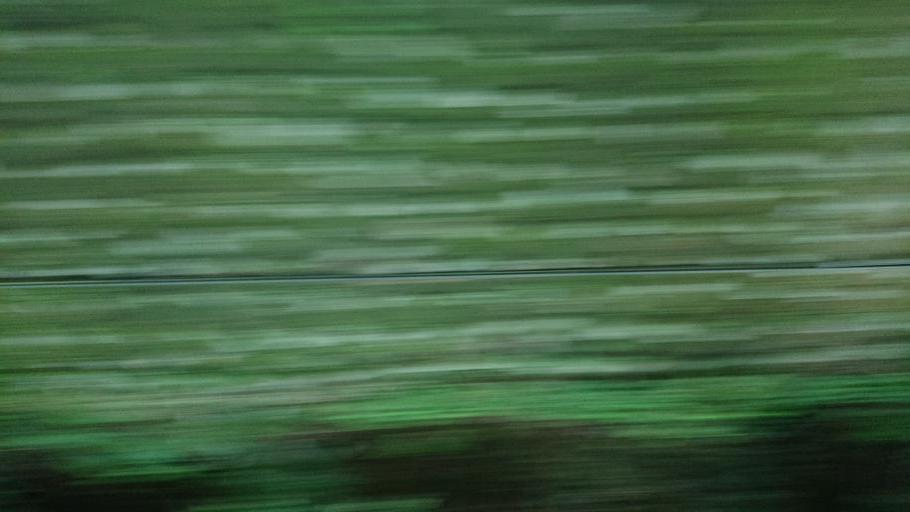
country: TW
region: Taiwan
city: Daxi
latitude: 24.8859
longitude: 121.3774
